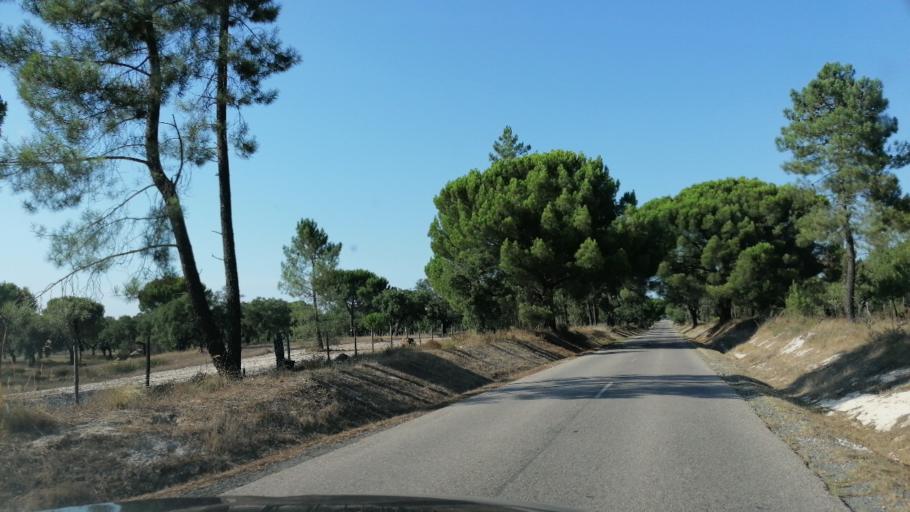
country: PT
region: Santarem
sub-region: Coruche
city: Coruche
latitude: 38.9086
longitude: -8.5267
